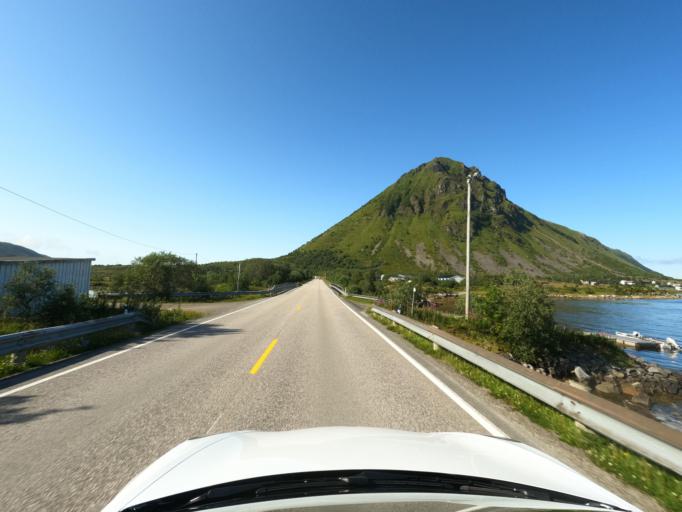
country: NO
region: Nordland
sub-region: Vestvagoy
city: Evjen
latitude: 68.2697
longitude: 13.9739
